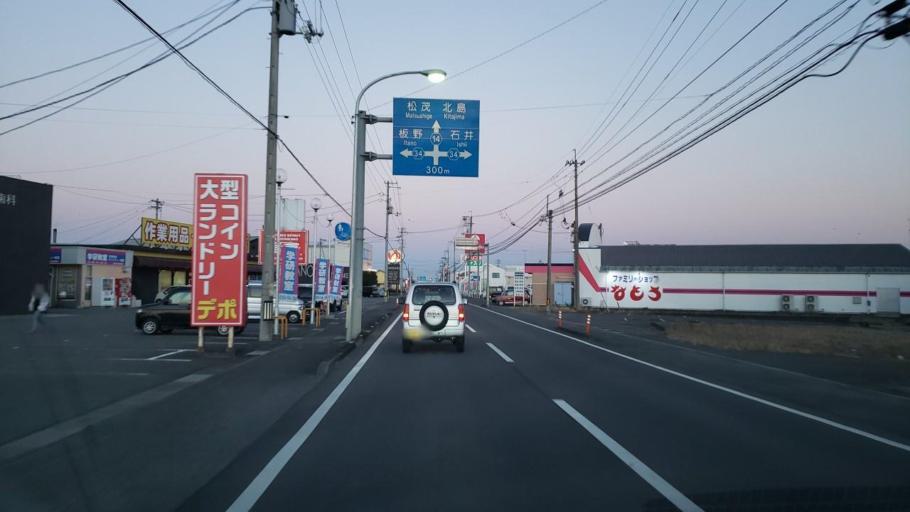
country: JP
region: Tokushima
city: Ishii
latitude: 34.1190
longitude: 134.4312
